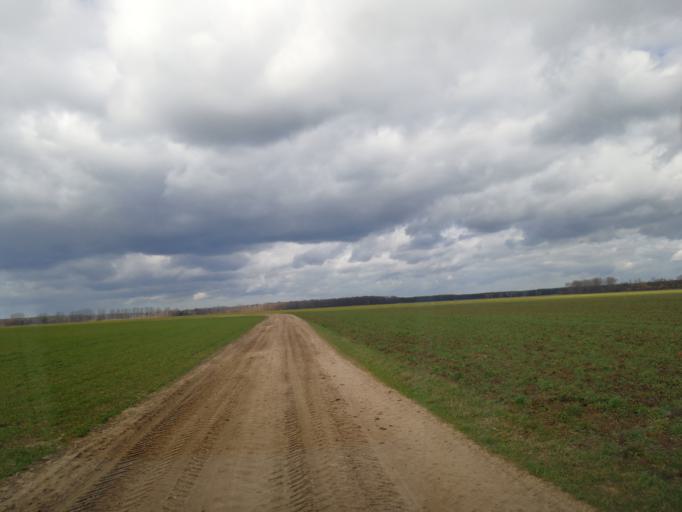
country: DE
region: Brandenburg
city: Schonewalde
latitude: 51.6831
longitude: 13.5558
